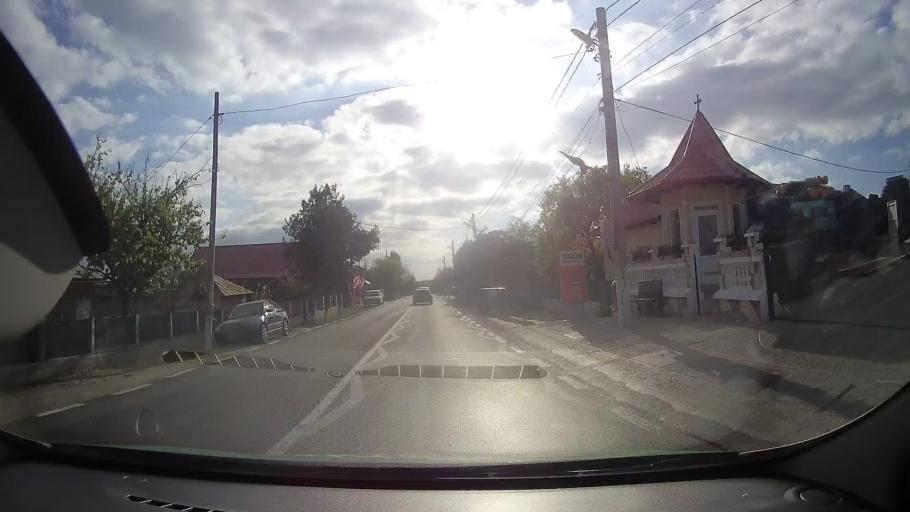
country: RO
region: Tulcea
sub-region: Comuna Topolog
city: Topolog
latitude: 44.8783
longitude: 28.3752
